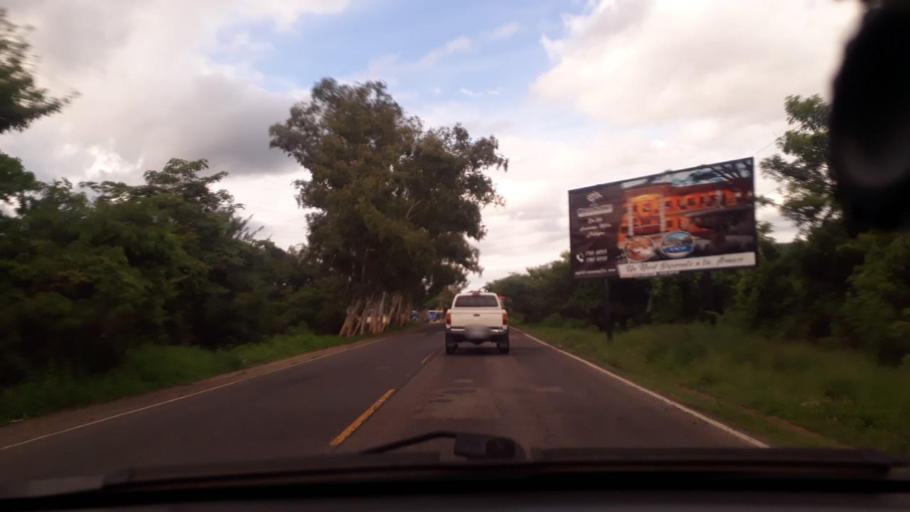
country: GT
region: Jutiapa
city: Jutiapa
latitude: 14.2824
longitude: -89.9531
